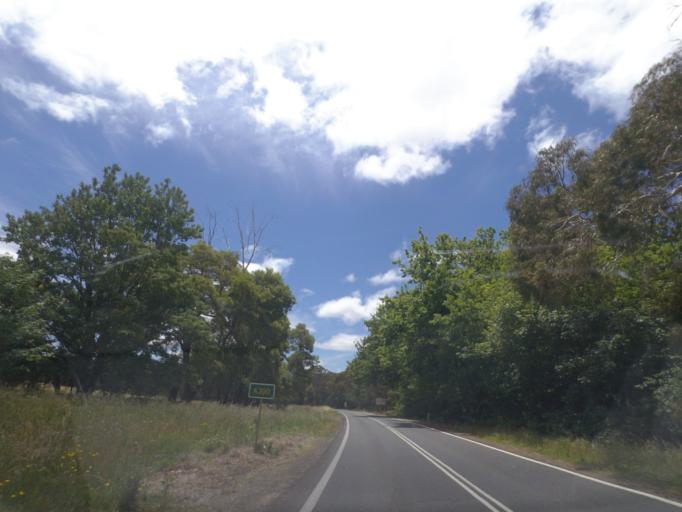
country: AU
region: Victoria
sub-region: Mount Alexander
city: Castlemaine
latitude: -37.3334
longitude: 144.1664
